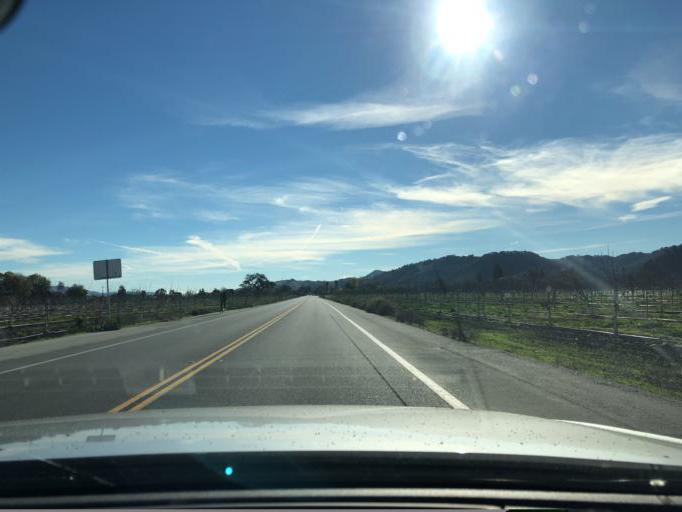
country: US
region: California
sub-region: Santa Clara County
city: Morgan Hill
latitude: 37.1800
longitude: -121.7204
